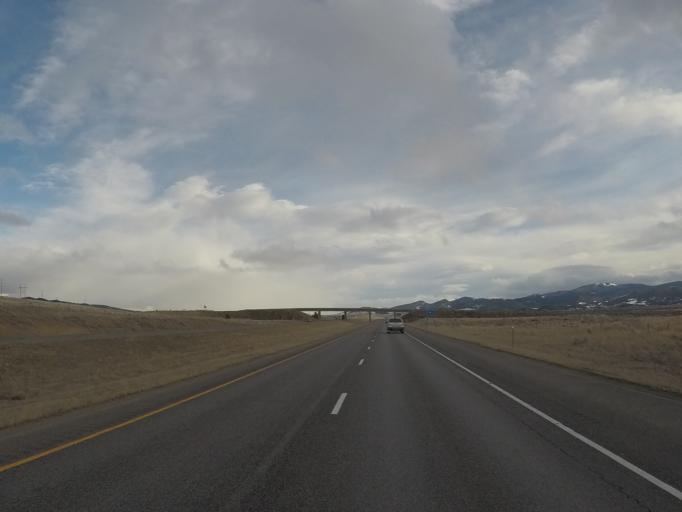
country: US
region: Montana
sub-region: Deer Lodge County
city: Warm Springs
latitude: 46.1106
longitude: -112.7981
